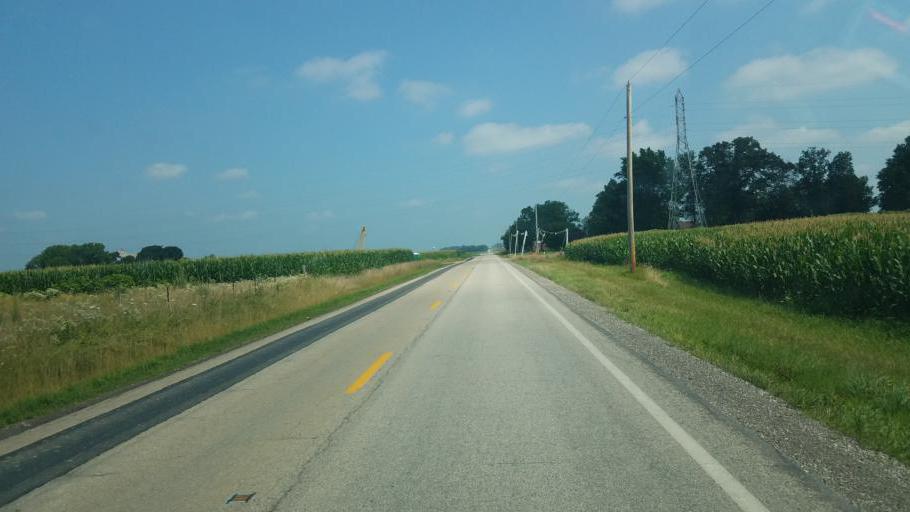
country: US
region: Ohio
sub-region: Crawford County
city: Bucyrus
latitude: 40.9267
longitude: -82.8542
